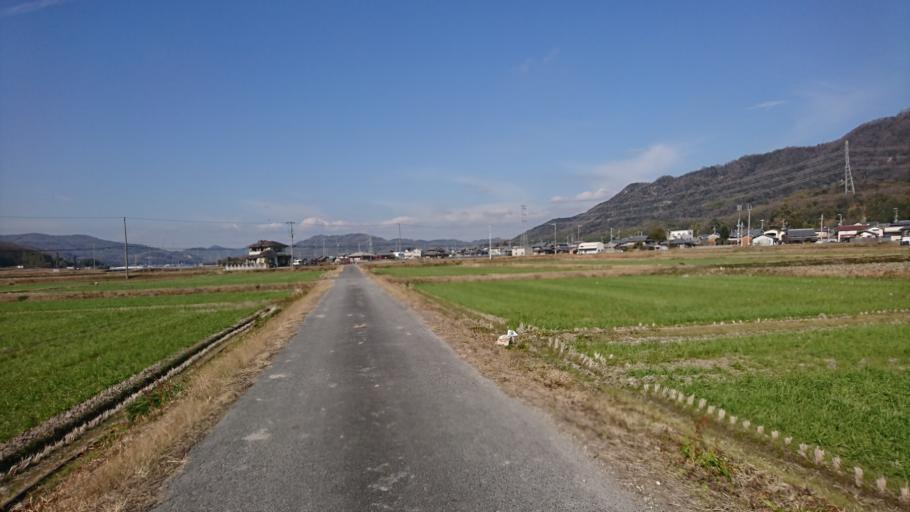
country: JP
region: Hyogo
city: Kakogawacho-honmachi
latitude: 34.8182
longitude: 134.8513
